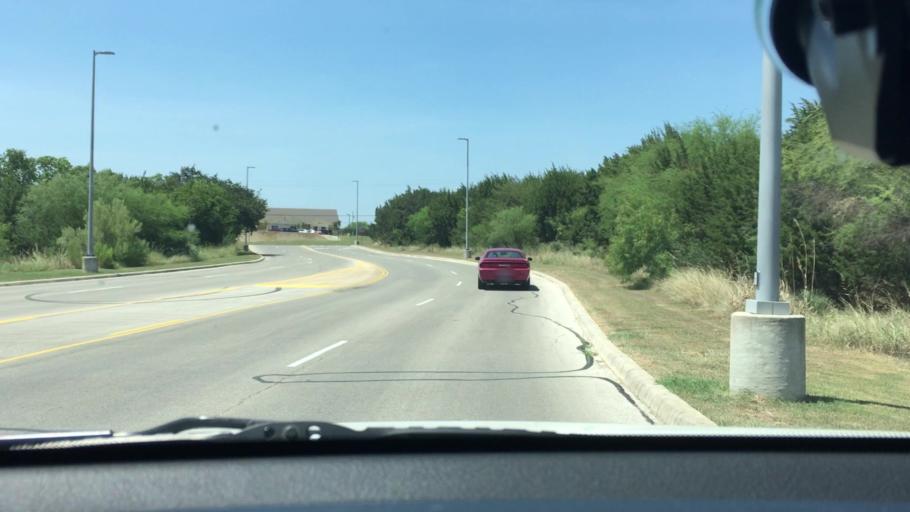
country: US
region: Texas
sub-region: Bexar County
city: Live Oak
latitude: 29.5513
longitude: -98.3254
